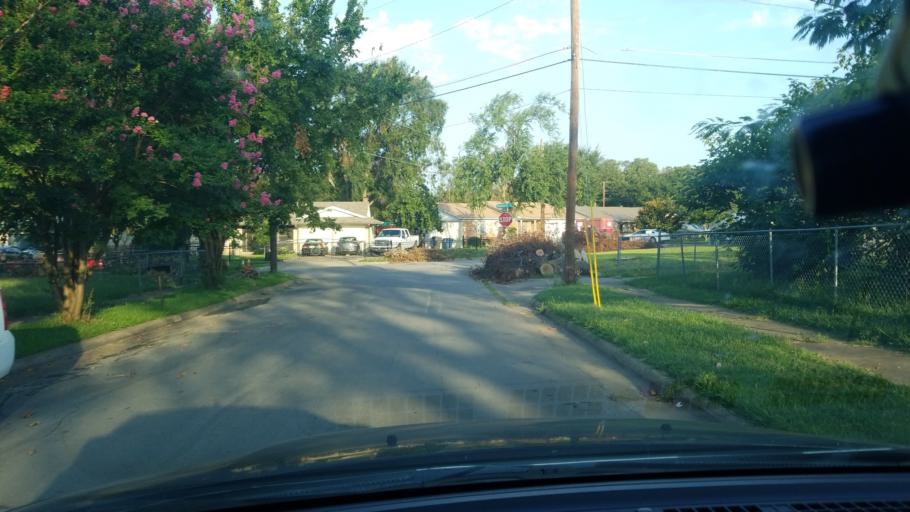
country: US
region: Texas
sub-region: Dallas County
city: Balch Springs
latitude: 32.7208
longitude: -96.6599
